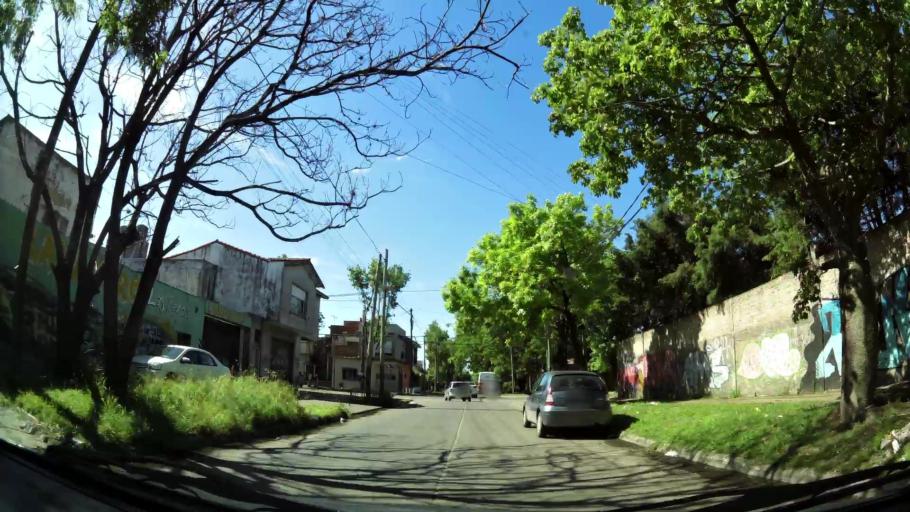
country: AR
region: Buenos Aires
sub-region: Partido de Lomas de Zamora
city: Lomas de Zamora
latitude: -34.7474
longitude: -58.4177
